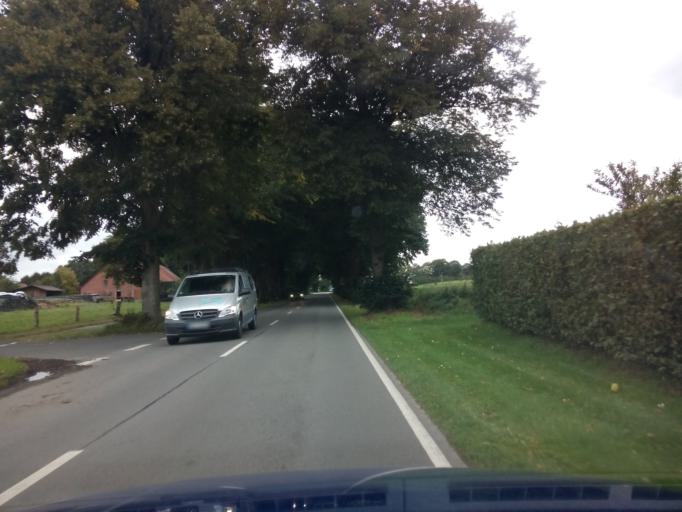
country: DE
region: Lower Saxony
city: Lubberstedt
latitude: 53.3349
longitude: 8.8069
